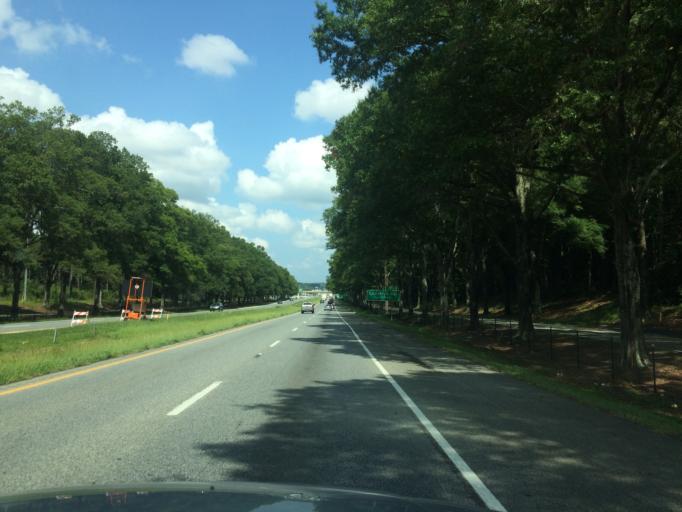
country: US
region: South Carolina
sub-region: Spartanburg County
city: Valley Falls
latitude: 34.9926
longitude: -81.9559
